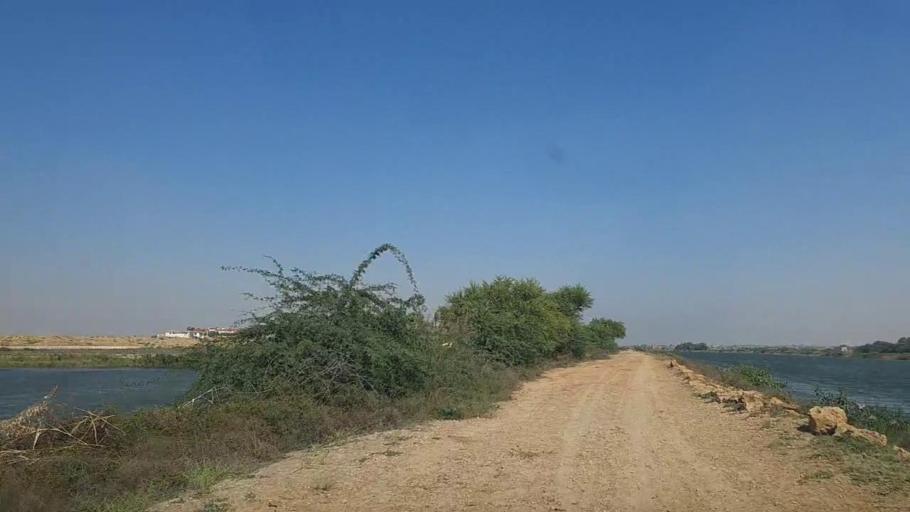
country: PK
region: Sindh
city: Thatta
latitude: 24.8111
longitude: 67.9863
